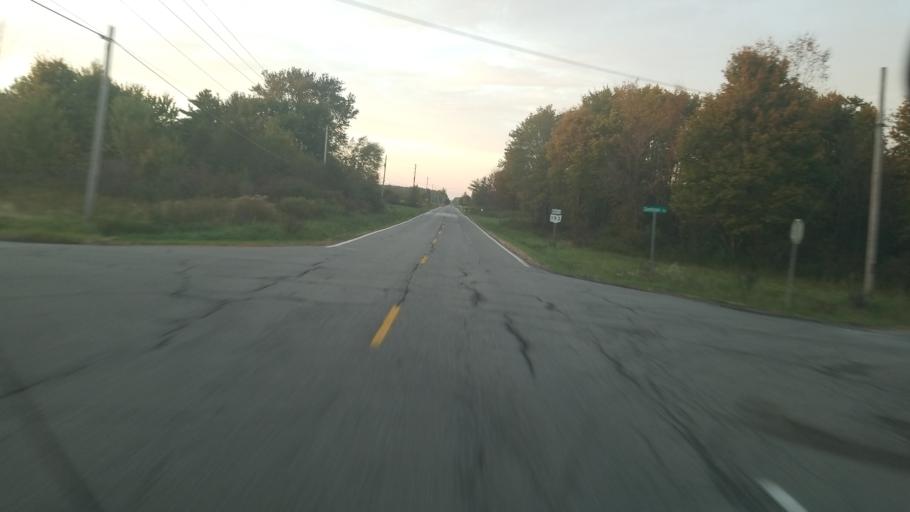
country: US
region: Ohio
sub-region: Ashtabula County
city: Andover
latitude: 41.6354
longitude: -80.6668
